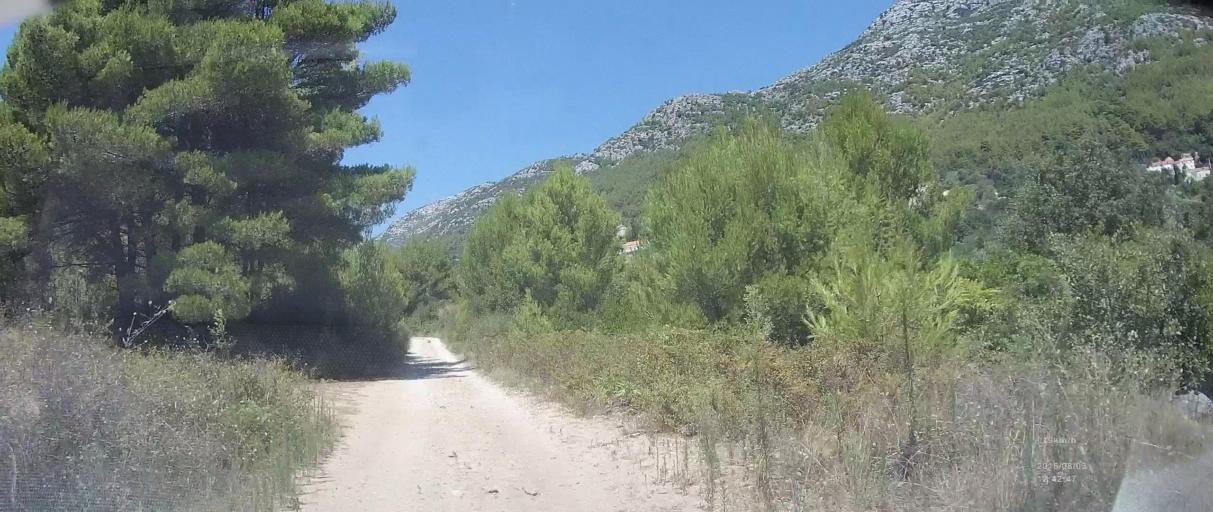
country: HR
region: Dubrovacko-Neretvanska
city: Blato
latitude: 42.7304
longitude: 17.5540
